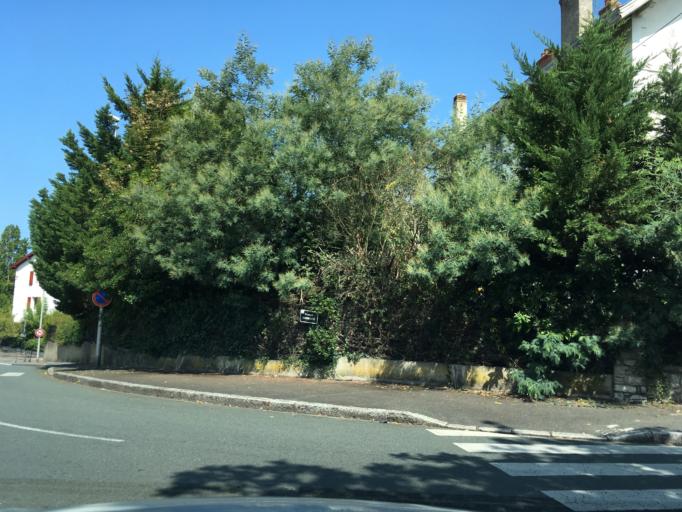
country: FR
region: Aquitaine
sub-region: Departement des Pyrenees-Atlantiques
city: Bayonne
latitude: 43.4906
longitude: -1.4867
